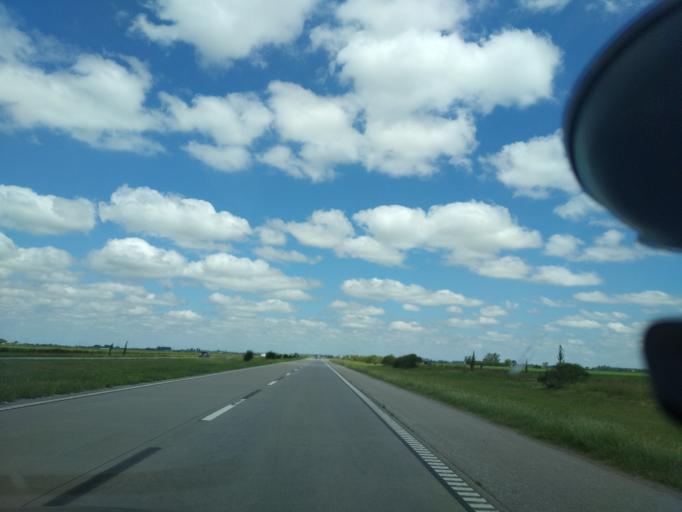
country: AR
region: Cordoba
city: Tio Pujio
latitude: -32.3172
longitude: -63.2755
